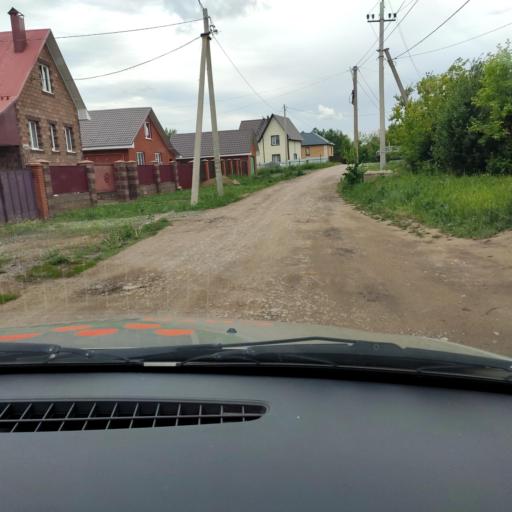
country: RU
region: Bashkortostan
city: Ufa
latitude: 54.6012
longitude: 55.9254
